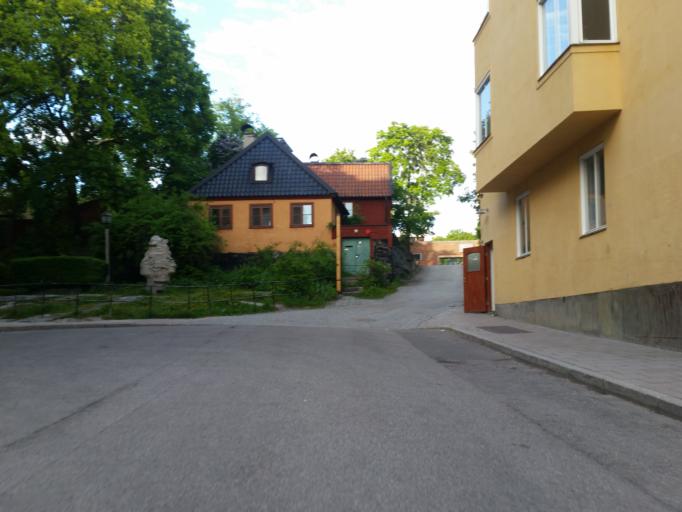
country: SE
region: Stockholm
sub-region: Stockholms Kommun
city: OEstermalm
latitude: 59.3168
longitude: 18.0811
